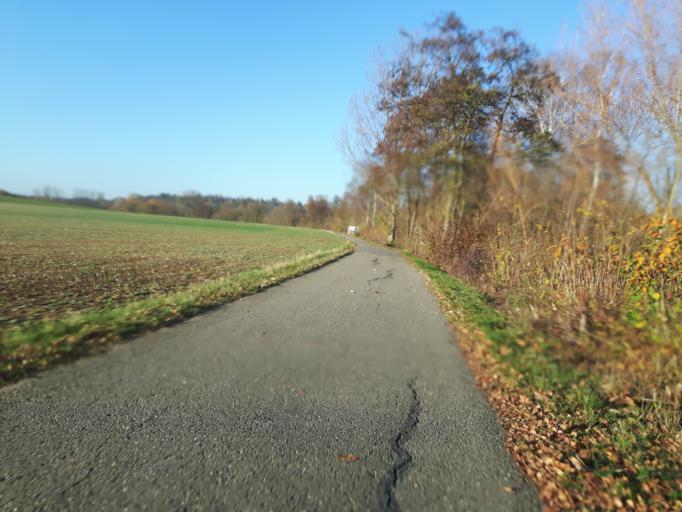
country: DE
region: Baden-Wuerttemberg
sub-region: Regierungsbezirk Stuttgart
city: Erlenbach
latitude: 49.1795
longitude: 9.2512
